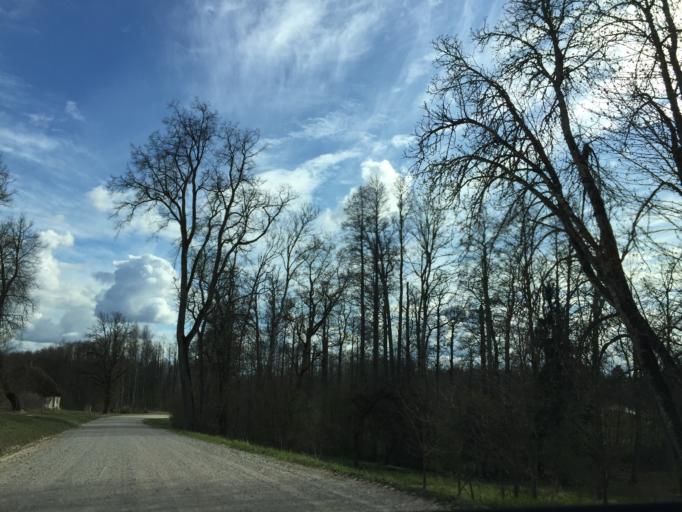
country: LV
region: Burtnieki
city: Matisi
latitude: 57.6133
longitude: 25.0797
